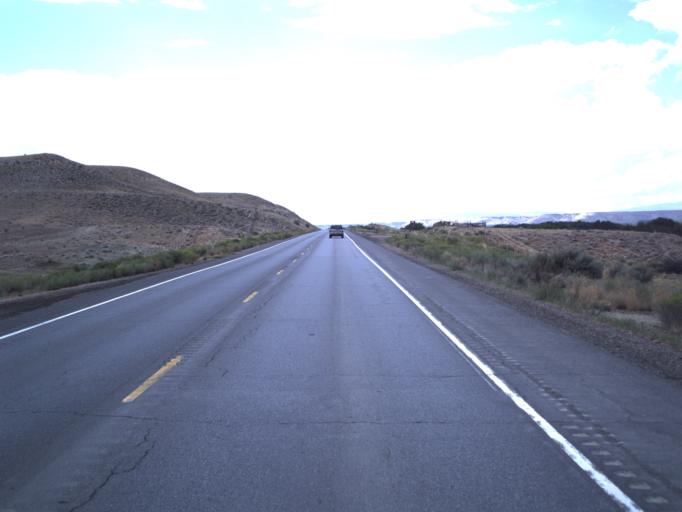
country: US
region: Utah
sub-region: Duchesne County
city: Duchesne
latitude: 40.1545
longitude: -110.2457
